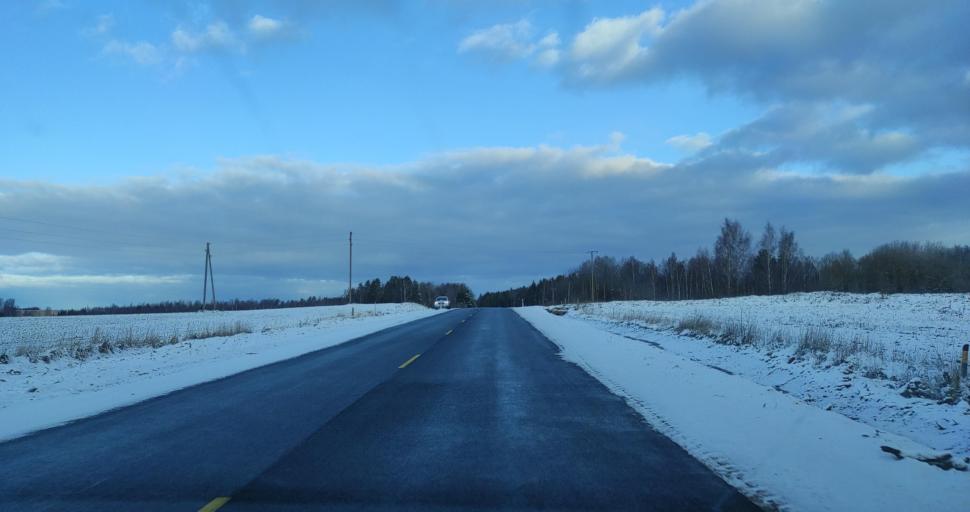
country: LV
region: Skrunda
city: Skrunda
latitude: 56.7195
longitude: 22.0090
